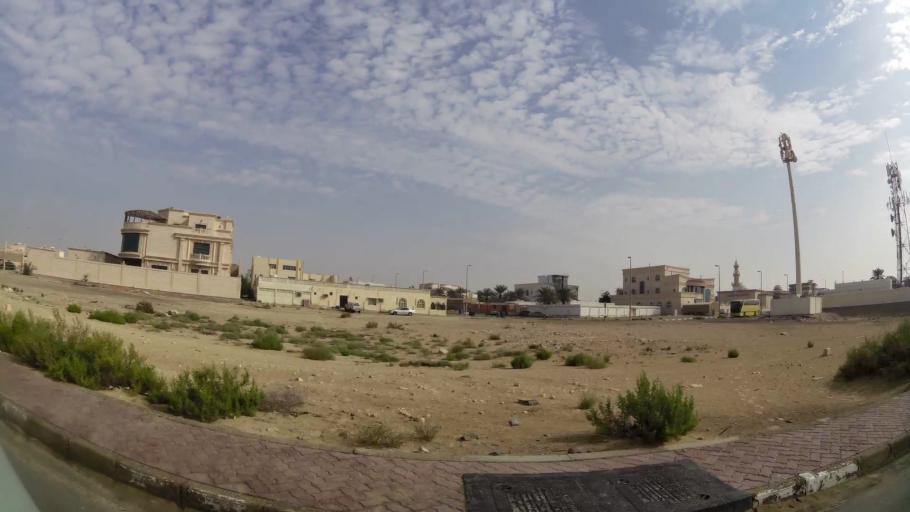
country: AE
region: Abu Dhabi
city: Abu Dhabi
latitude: 24.2572
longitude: 54.7056
